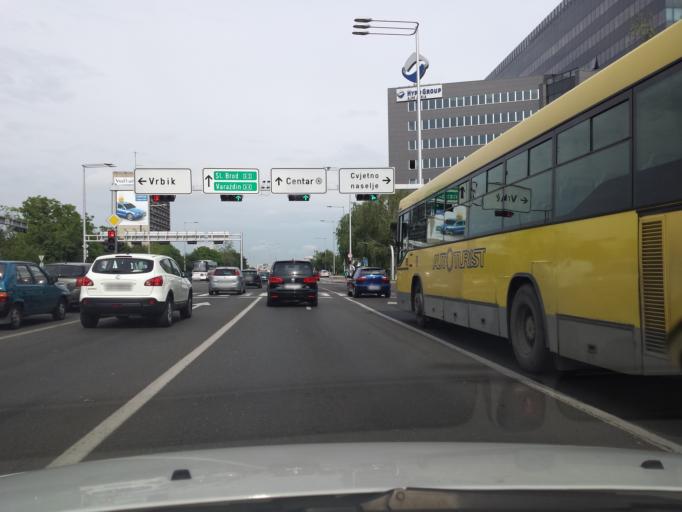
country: HR
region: Grad Zagreb
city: Novi Zagreb
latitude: 45.7942
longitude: 15.9683
